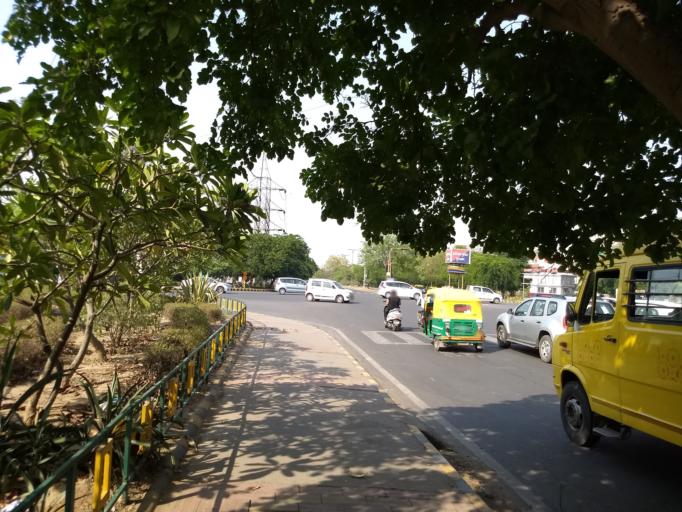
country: IN
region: Haryana
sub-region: Gurgaon
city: Gurgaon
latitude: 28.4344
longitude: 77.0488
